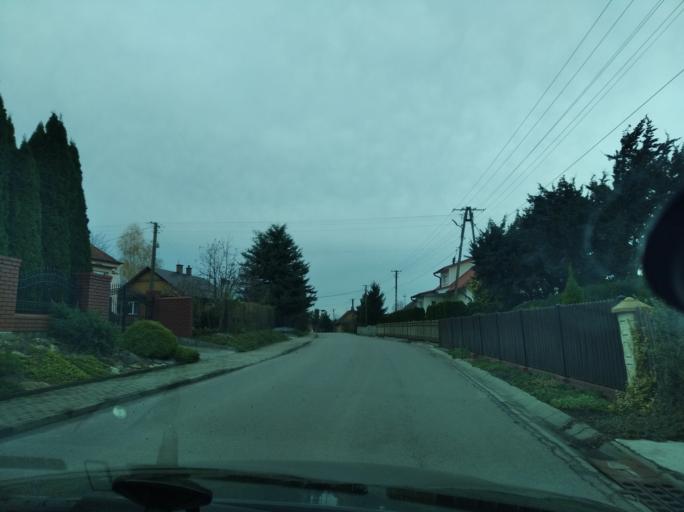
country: PL
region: Subcarpathian Voivodeship
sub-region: Powiat przeworski
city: Debow
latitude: 50.0460
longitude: 22.4293
